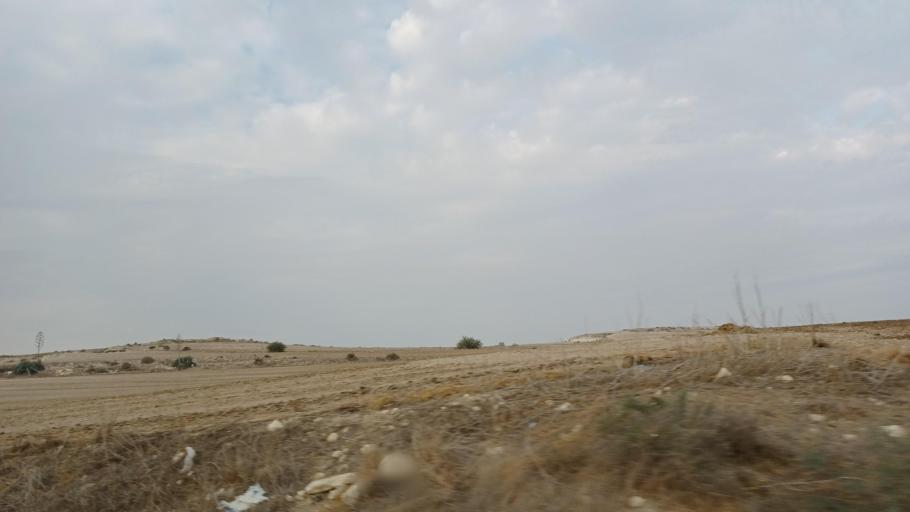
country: CY
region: Larnaka
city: Athienou
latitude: 35.0333
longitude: 33.5722
